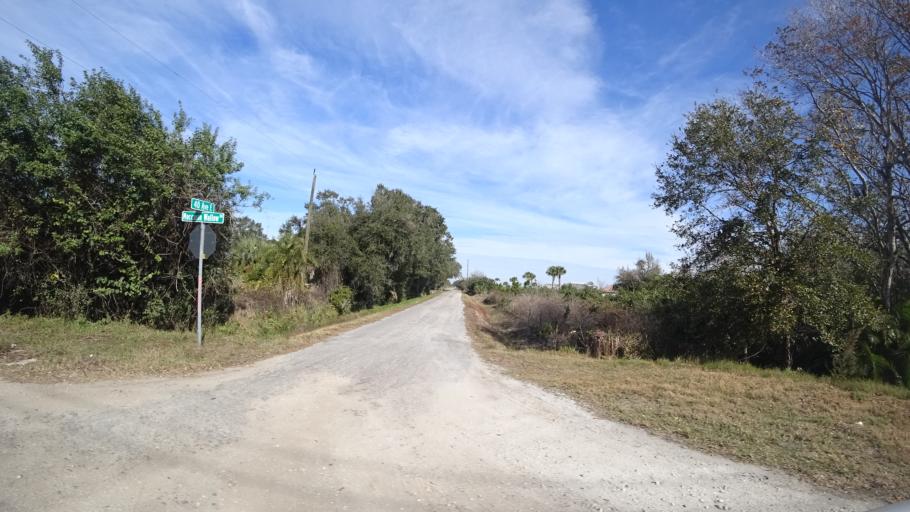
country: US
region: Florida
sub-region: Manatee County
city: Memphis
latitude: 27.6014
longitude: -82.5229
